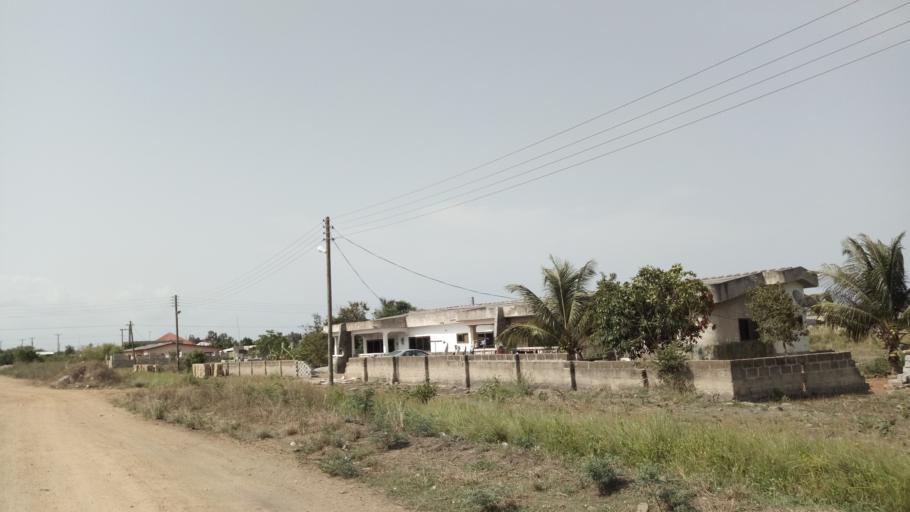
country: GH
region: Central
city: Winneba
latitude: 5.3738
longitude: -0.6496
